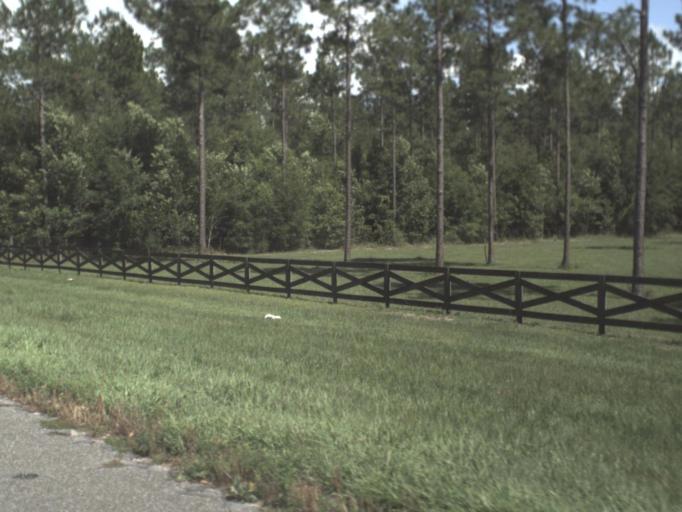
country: US
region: Florida
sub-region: Lafayette County
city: Mayo
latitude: 30.0529
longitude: -83.1435
